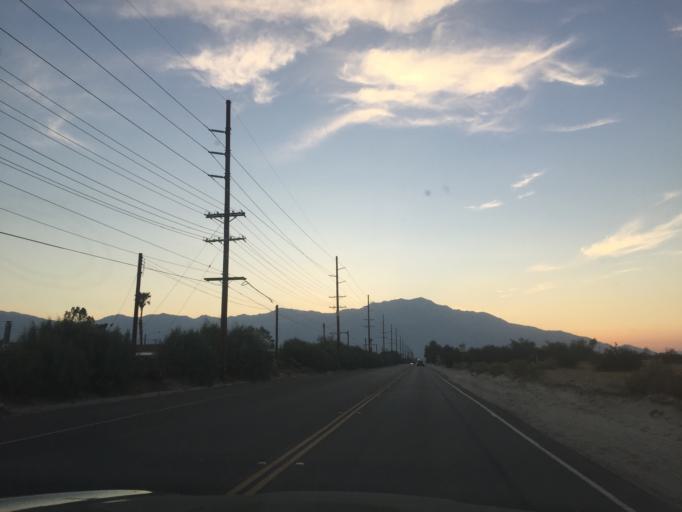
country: US
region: California
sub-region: Riverside County
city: Thousand Palms
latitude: 33.8165
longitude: -116.3755
